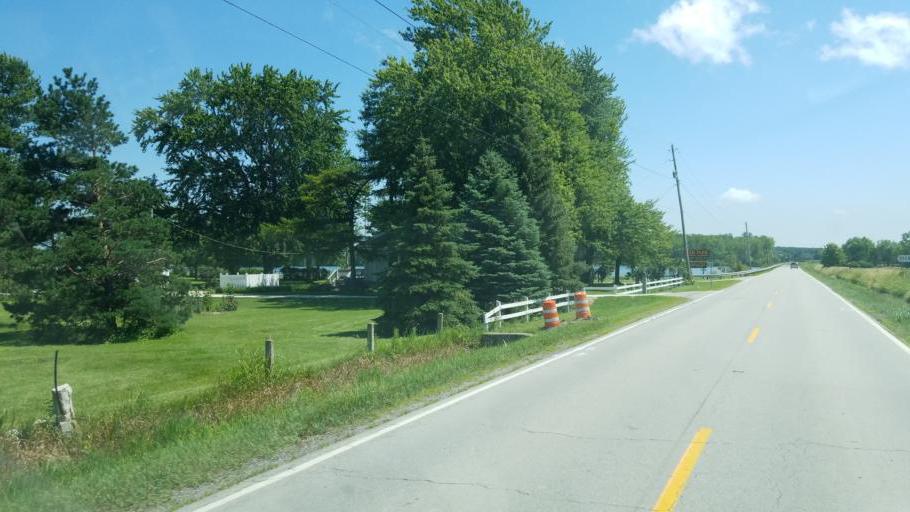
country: US
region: Ohio
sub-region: Erie County
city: Sandusky
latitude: 41.4516
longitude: -82.8157
